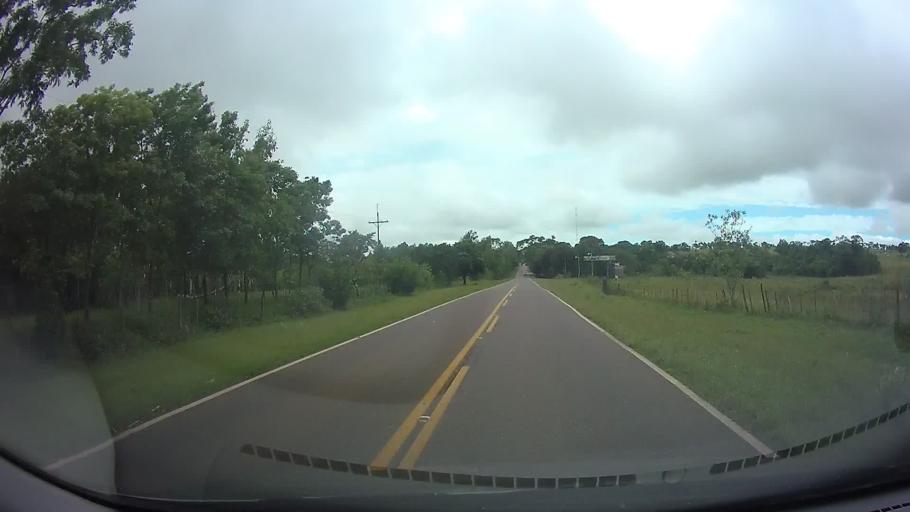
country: PY
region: Paraguari
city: Acahay
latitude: -25.9431
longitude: -57.0969
